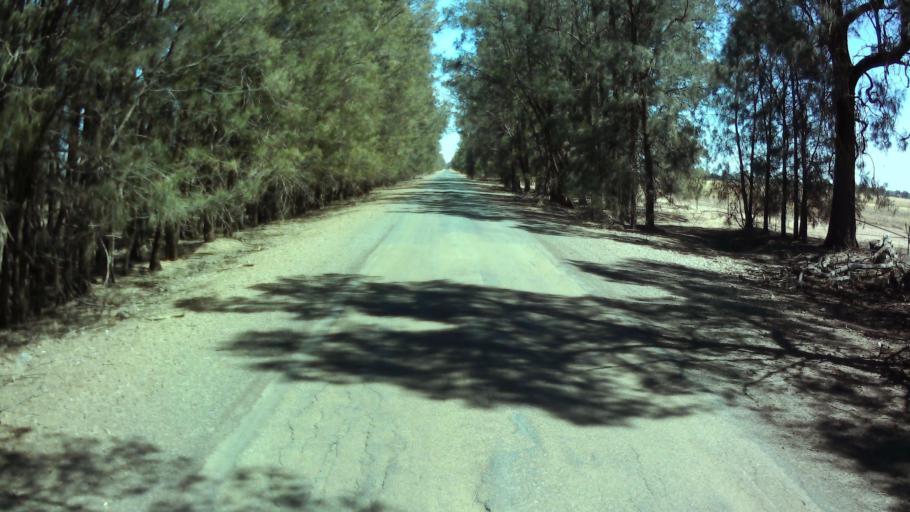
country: AU
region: New South Wales
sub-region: Weddin
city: Grenfell
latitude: -33.8835
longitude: 147.6896
